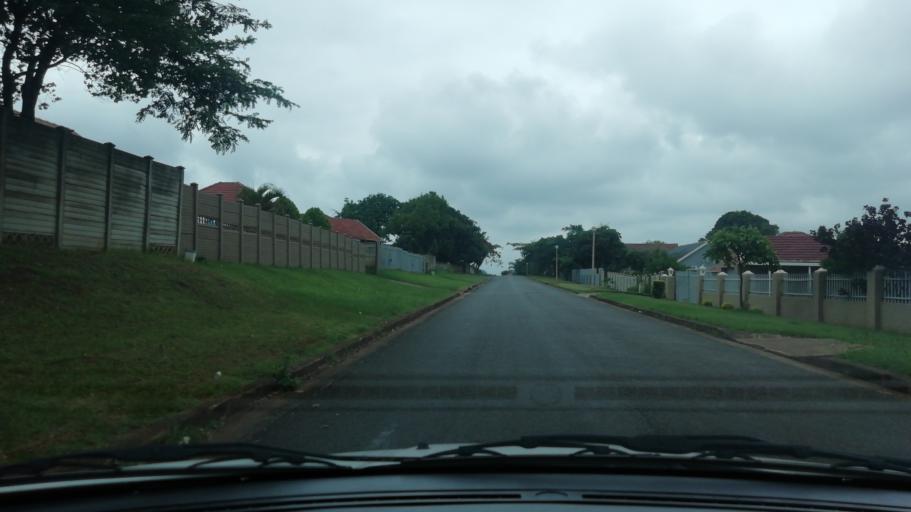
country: ZA
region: KwaZulu-Natal
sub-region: uThungulu District Municipality
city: Empangeni
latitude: -28.7605
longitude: 31.9006
